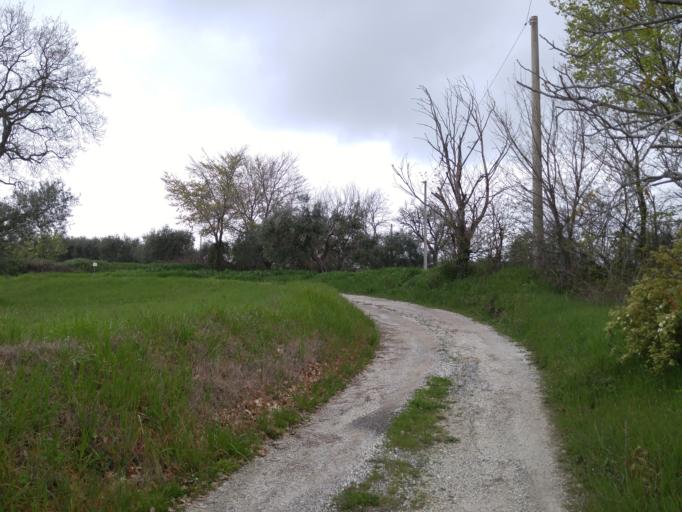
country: IT
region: The Marches
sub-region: Provincia di Pesaro e Urbino
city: Saltara
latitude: 43.7668
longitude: 12.9064
